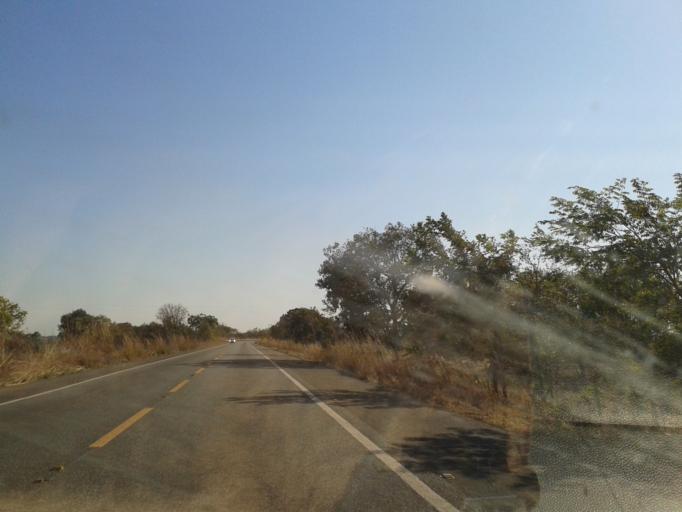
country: BR
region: Goias
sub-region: Mozarlandia
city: Mozarlandia
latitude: -14.9220
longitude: -50.5534
